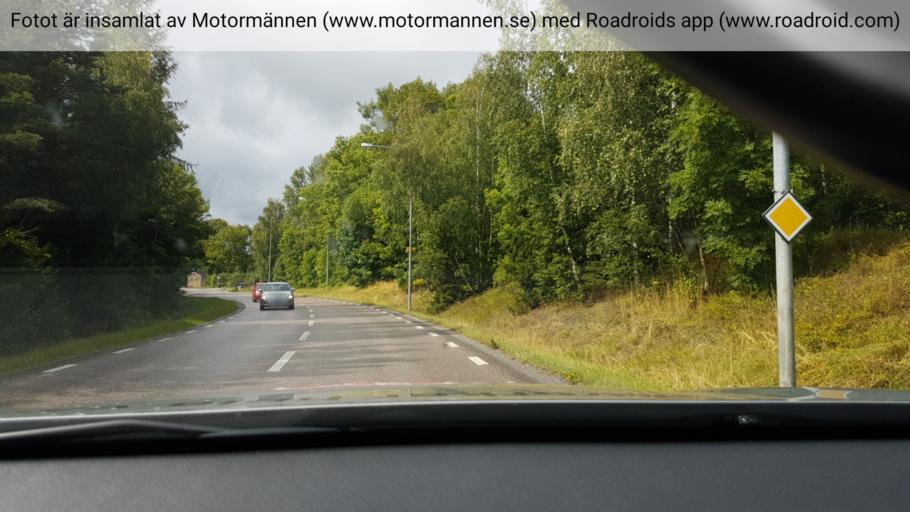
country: SE
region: Stockholm
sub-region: Norrtalje Kommun
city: Rimbo
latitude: 59.7377
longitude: 18.4996
